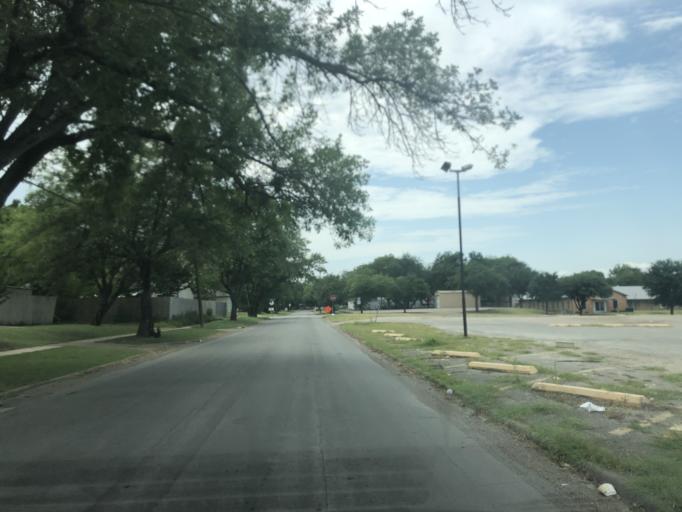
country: US
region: Texas
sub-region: Dallas County
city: Grand Prairie
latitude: 32.7356
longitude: -97.0069
